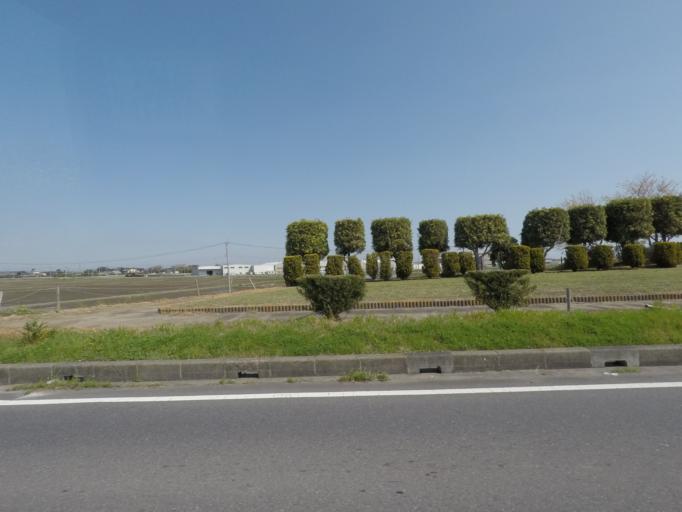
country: JP
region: Chiba
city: Katori-shi
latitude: 35.9193
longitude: 140.4698
